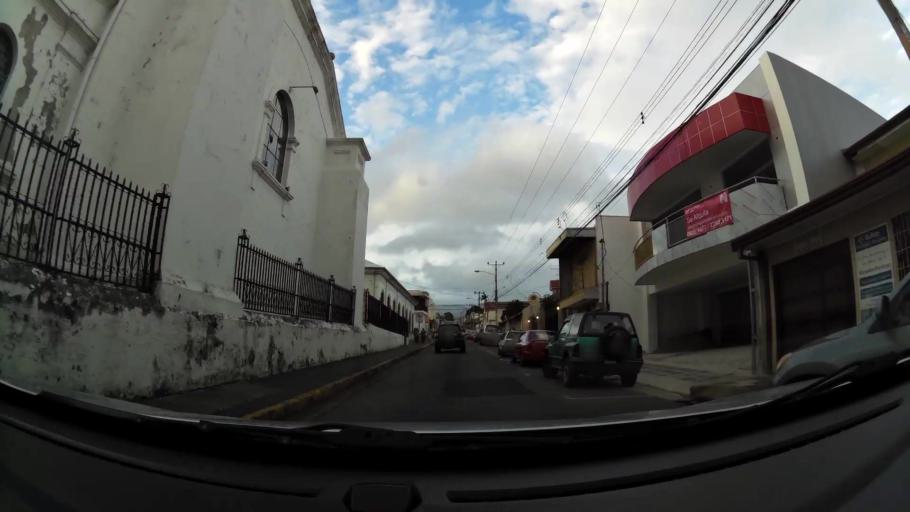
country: CR
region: Heredia
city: Heredia
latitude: 9.9981
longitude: -84.1159
